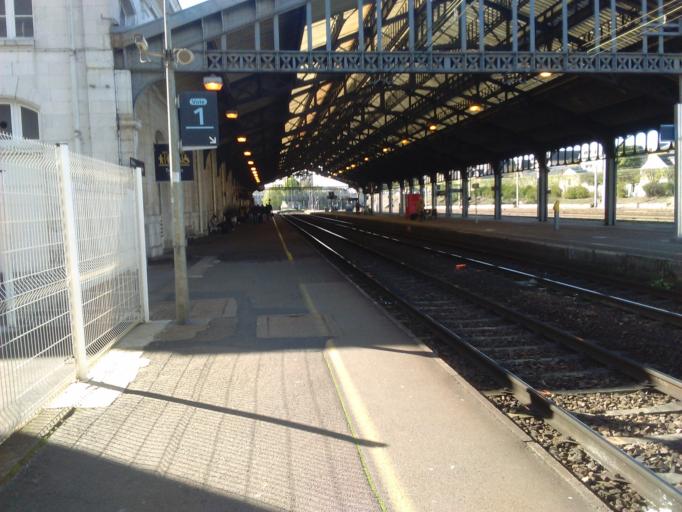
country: FR
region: Centre
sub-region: Departement du Loir-et-Cher
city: Blois
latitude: 47.5861
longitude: 1.3235
